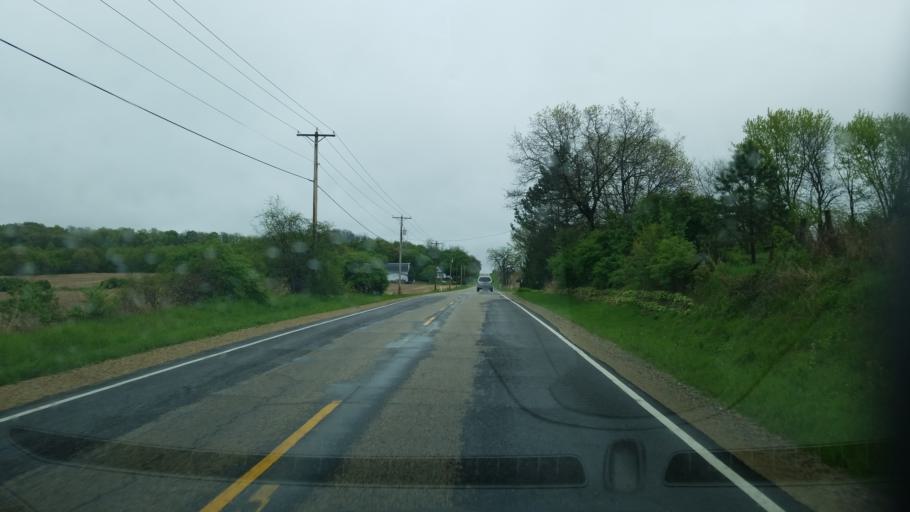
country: US
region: Wisconsin
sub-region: Dane County
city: Oregon
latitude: 42.9291
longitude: -89.4271
